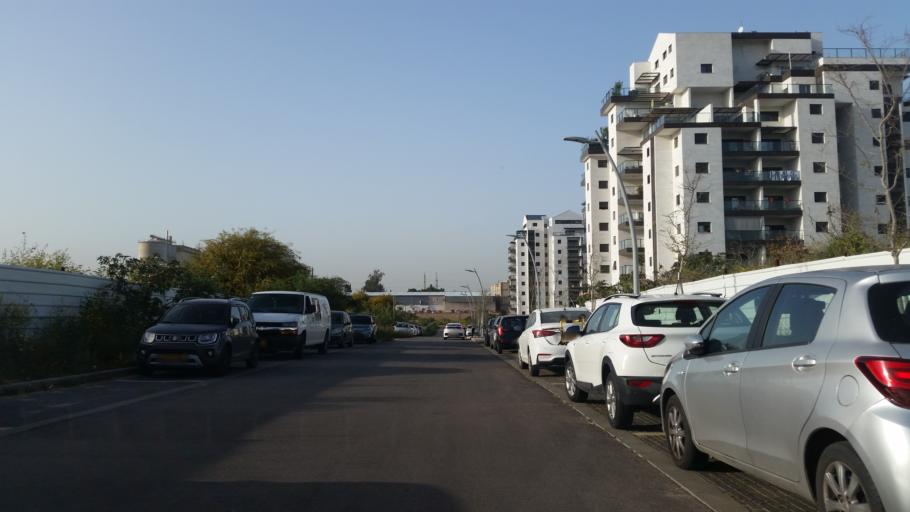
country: IL
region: Central District
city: Ra'anana
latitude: 32.1951
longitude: 34.8884
